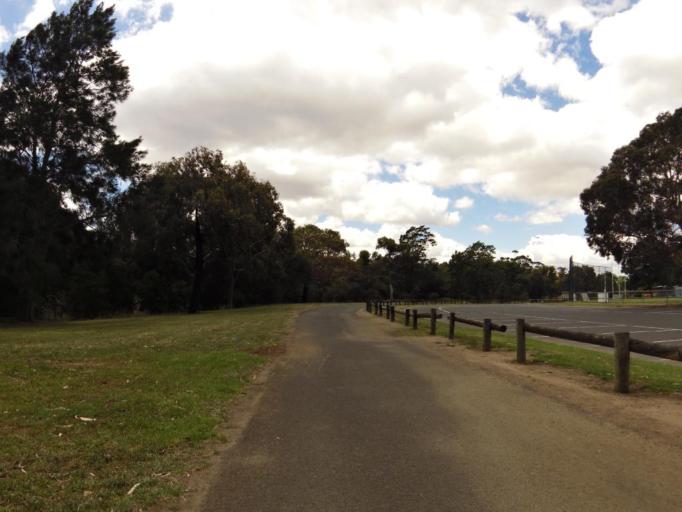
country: AU
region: Victoria
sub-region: Hume
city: Westmeadows
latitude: -37.6751
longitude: 144.8827
